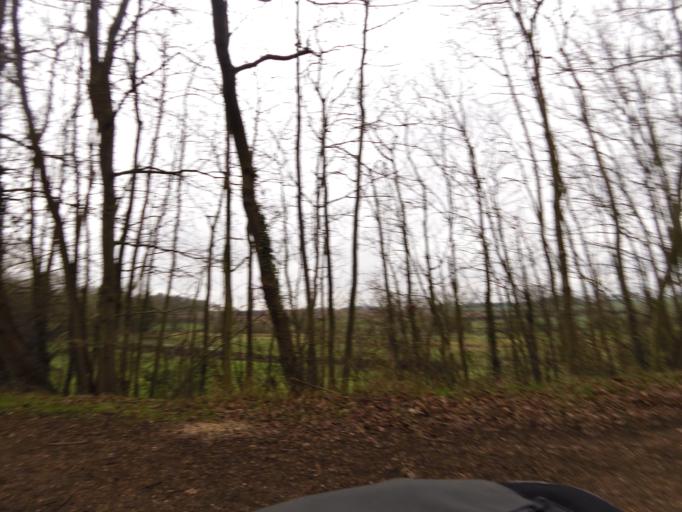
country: GB
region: England
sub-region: Norfolk
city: Briston
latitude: 52.7530
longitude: 1.0976
